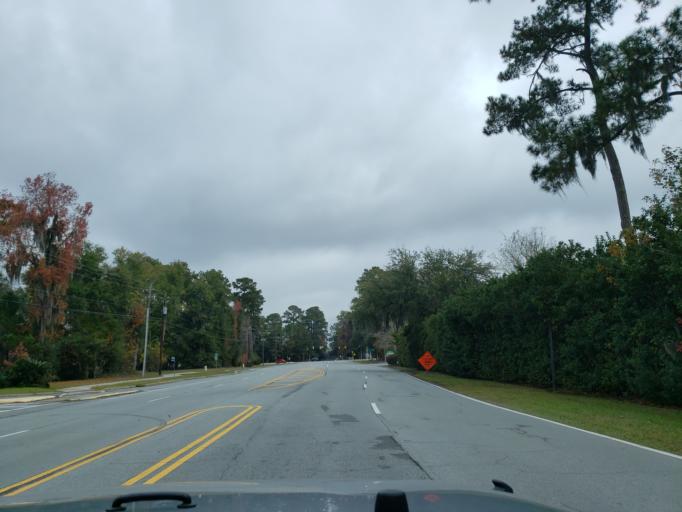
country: US
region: Georgia
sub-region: Chatham County
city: Whitemarsh Island
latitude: 32.0350
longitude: -80.9916
